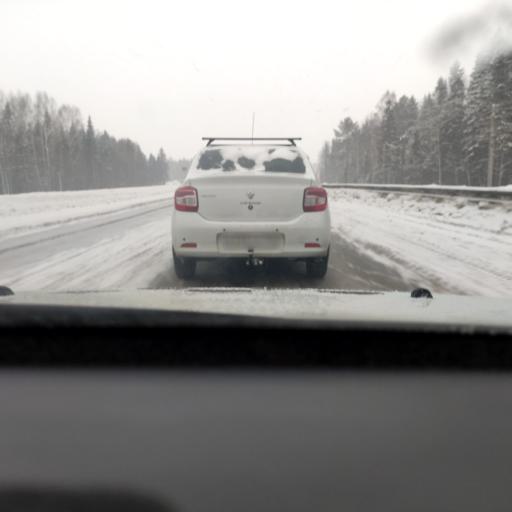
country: RU
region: Perm
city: Polazna
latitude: 58.1464
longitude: 56.4194
